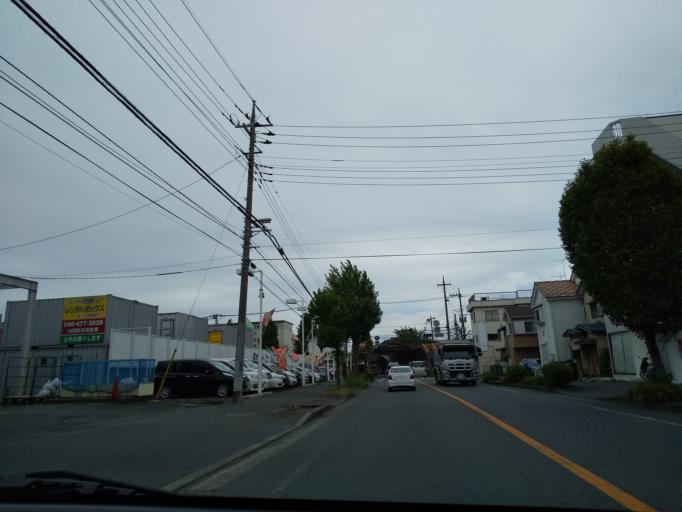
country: JP
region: Kanagawa
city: Zama
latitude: 35.5145
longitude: 139.4068
